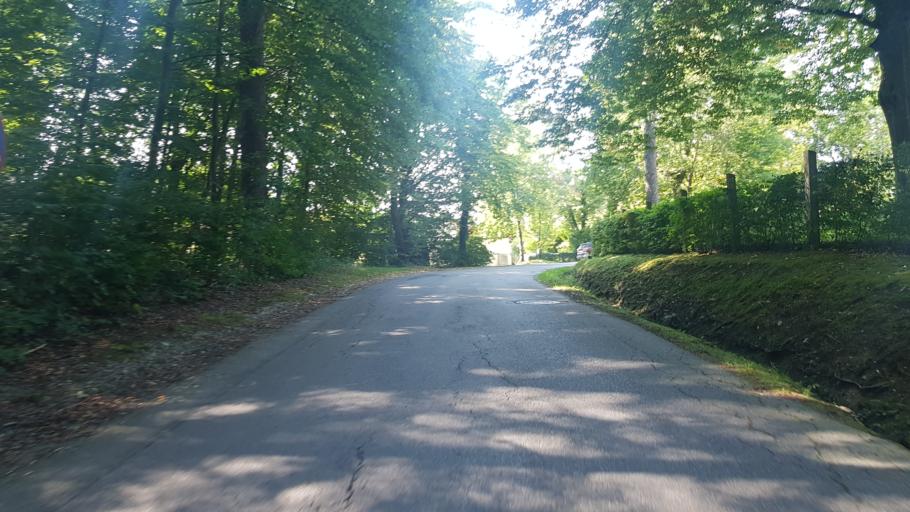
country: DE
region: Bavaria
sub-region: Upper Bavaria
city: Herrsching am Ammersee
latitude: 48.0088
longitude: 11.1644
